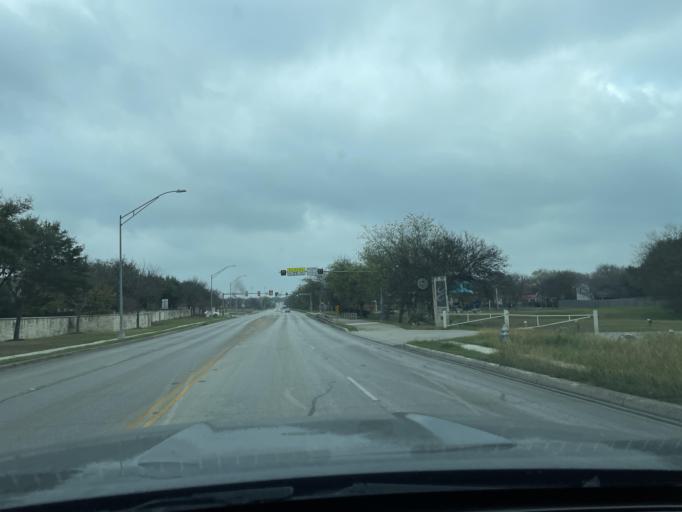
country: US
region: Texas
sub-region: Bexar County
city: Leon Valley
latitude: 29.5572
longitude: -98.6265
